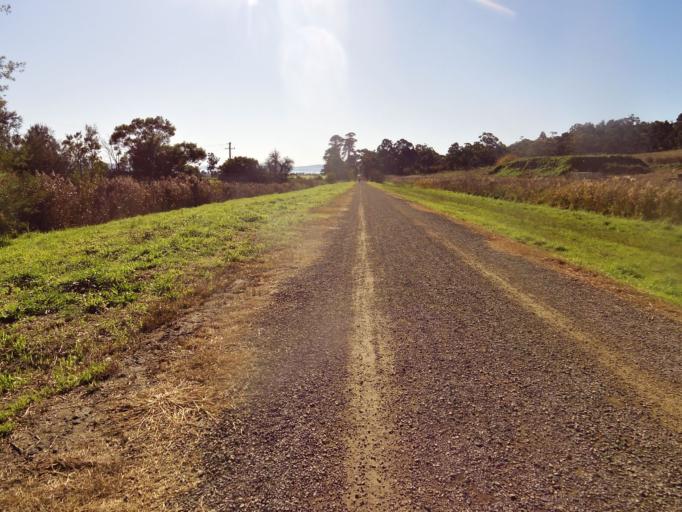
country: AU
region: Victoria
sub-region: Yarra Ranges
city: Lilydale
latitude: -37.7416
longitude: 145.3603
